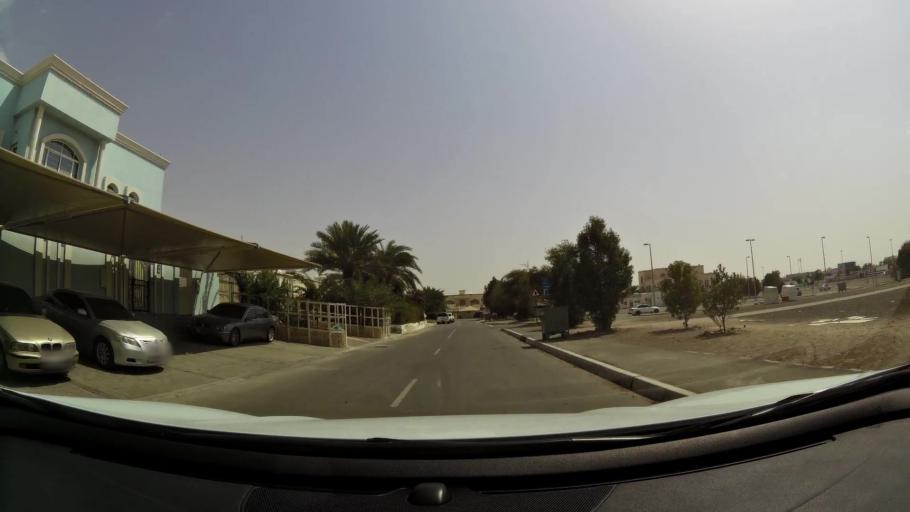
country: AE
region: Abu Dhabi
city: Abu Dhabi
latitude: 24.2937
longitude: 54.6464
